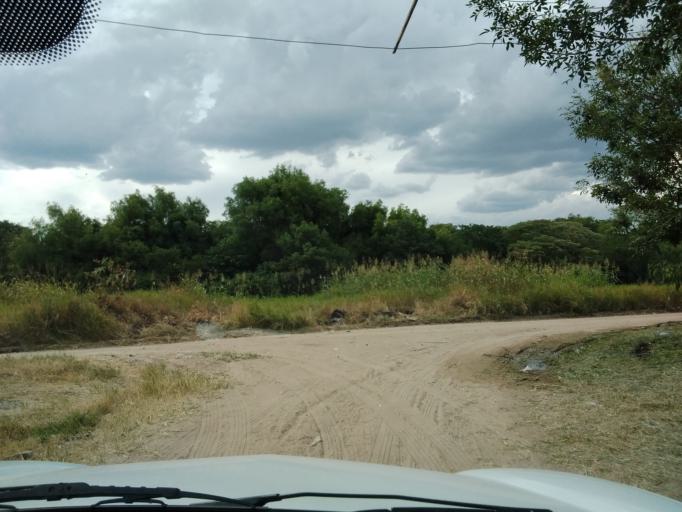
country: AR
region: Corrientes
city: Corrientes
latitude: -27.5209
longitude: -58.7954
